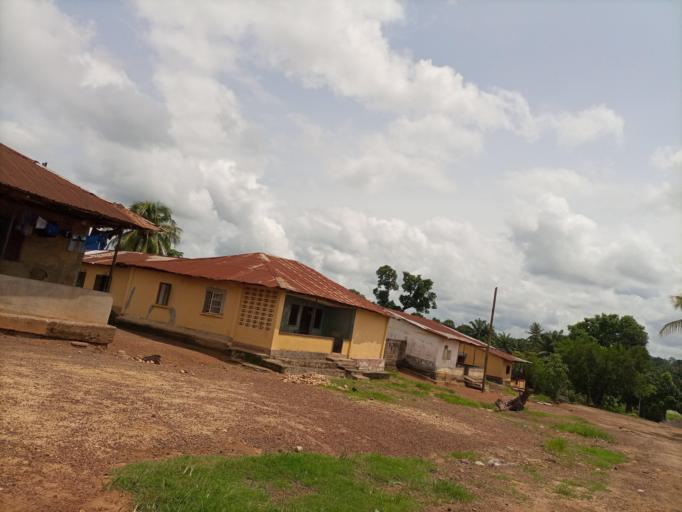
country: SL
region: Southern Province
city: Bo
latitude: 7.9591
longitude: -11.7577
